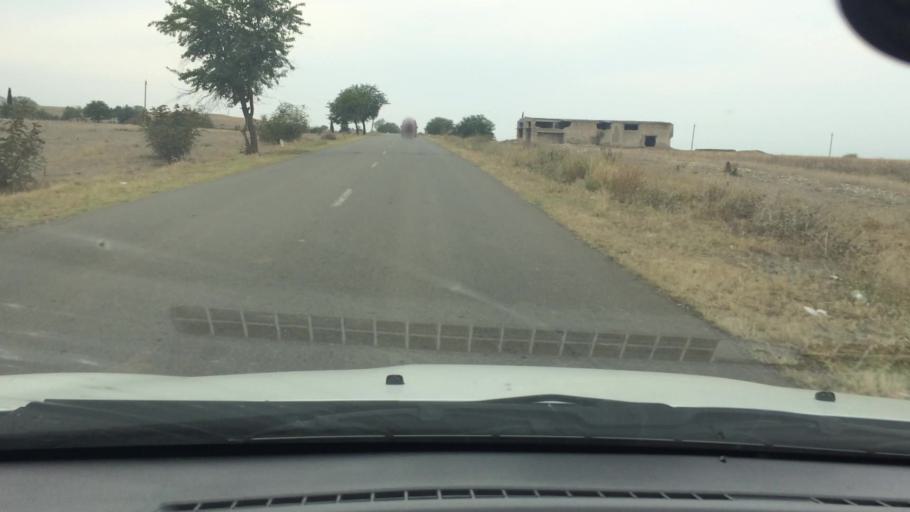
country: AM
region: Tavush
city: Berdavan
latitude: 41.3369
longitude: 45.0148
